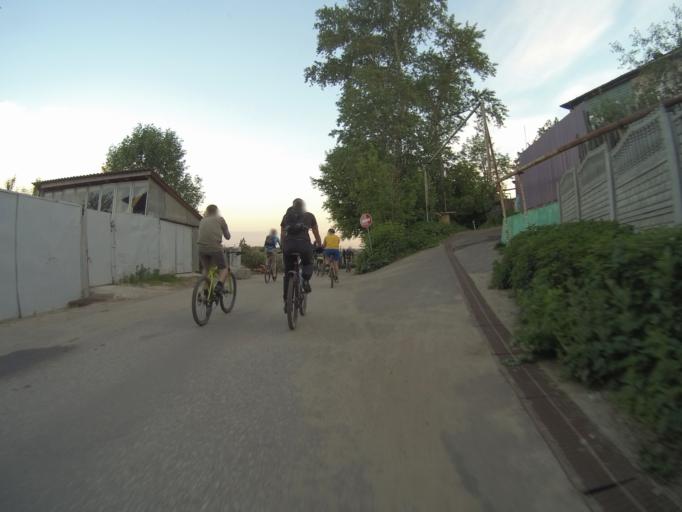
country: RU
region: Vladimir
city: Vladimir
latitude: 56.1267
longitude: 40.4120
